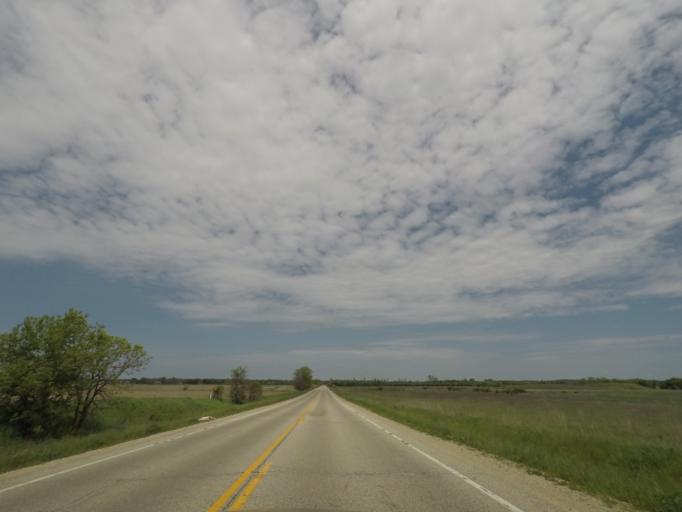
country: US
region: Wisconsin
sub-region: Rock County
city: Evansville
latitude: 42.7563
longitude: -89.2990
